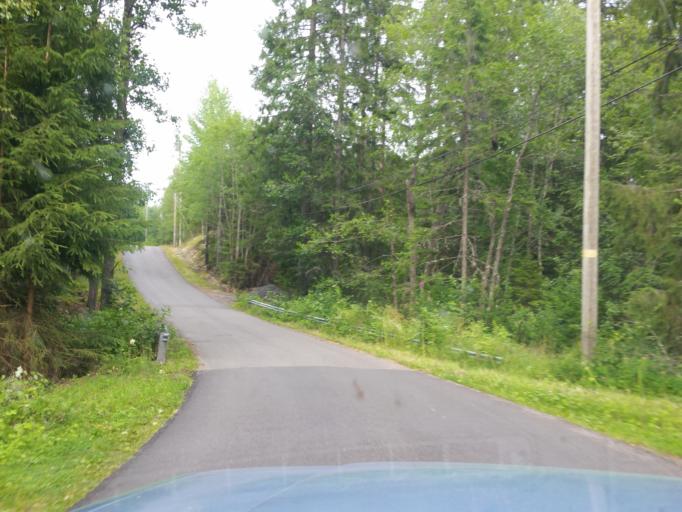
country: FI
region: Uusimaa
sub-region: Helsinki
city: Kaerkoelae
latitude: 60.5538
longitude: 23.9938
